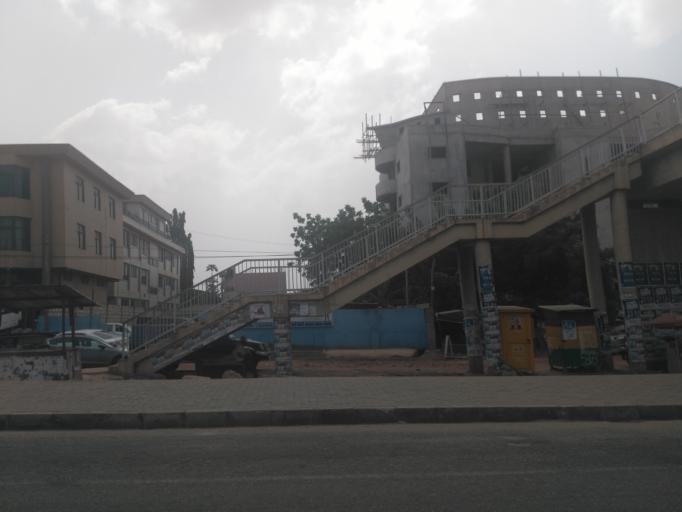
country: GH
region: Greater Accra
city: Dome
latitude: 5.6138
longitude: -0.2228
